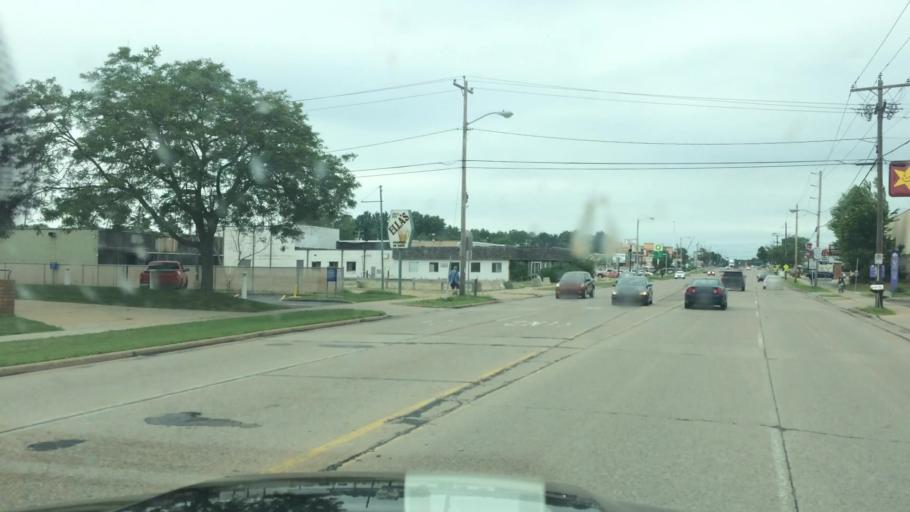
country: US
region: Wisconsin
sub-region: Portage County
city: Stevens Point
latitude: 44.5290
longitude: -89.5747
